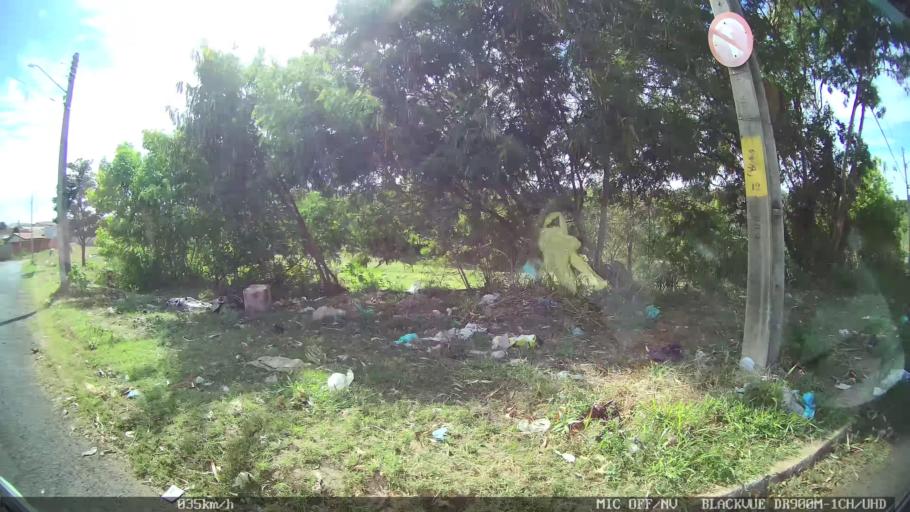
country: BR
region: Sao Paulo
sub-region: Catanduva
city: Catanduva
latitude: -21.1266
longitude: -48.9442
